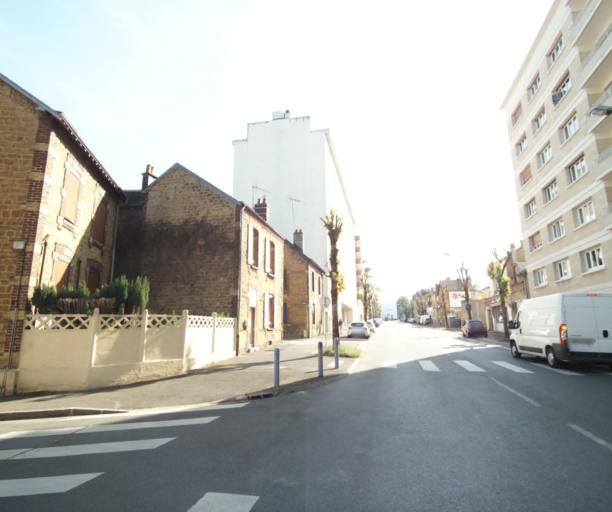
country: FR
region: Champagne-Ardenne
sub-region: Departement des Ardennes
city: Charleville-Mezieres
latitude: 49.7749
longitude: 4.7078
